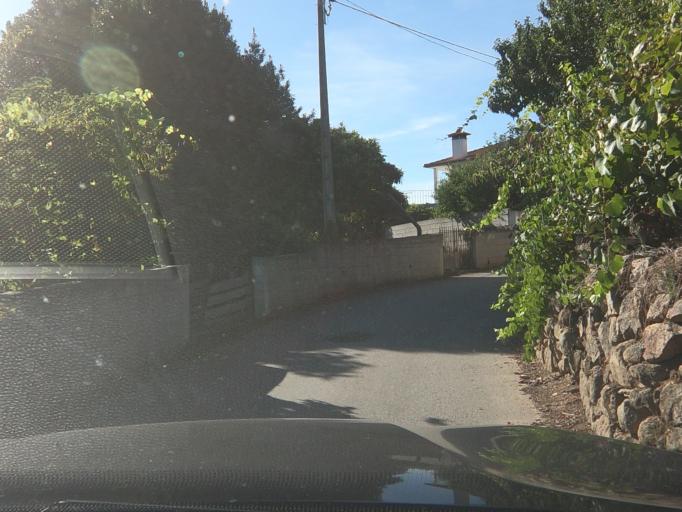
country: PT
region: Vila Real
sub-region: Vila Real
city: Vila Real
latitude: 41.2811
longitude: -7.7430
